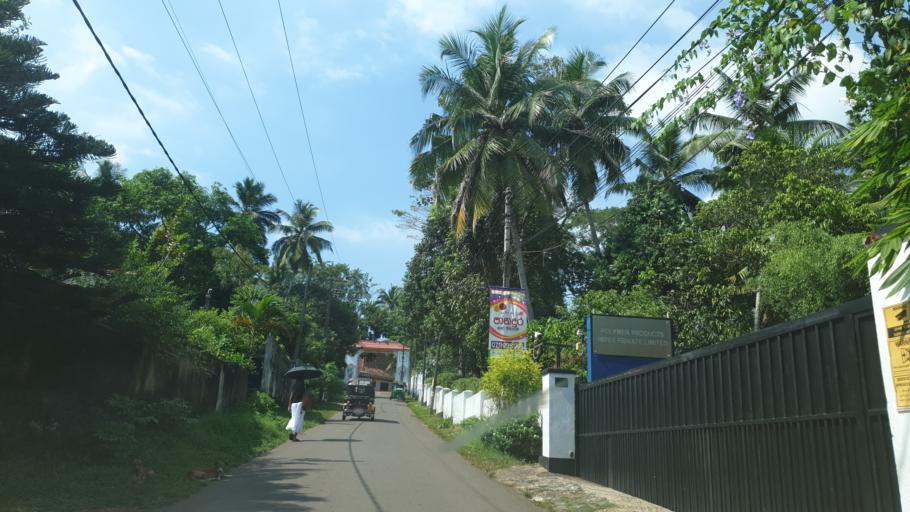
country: LK
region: Western
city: Panadura
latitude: 6.7224
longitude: 79.9571
